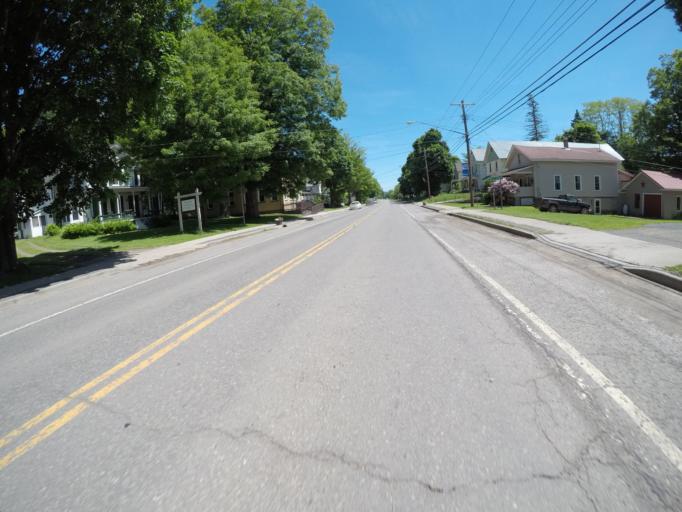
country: US
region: New York
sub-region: Delaware County
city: Delhi
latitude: 42.1921
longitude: -74.9933
